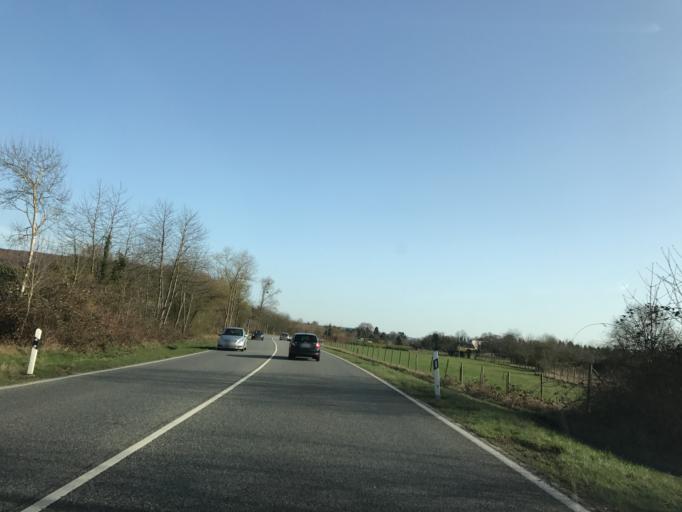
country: DE
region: Rheinland-Pfalz
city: Unkel
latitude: 50.5895
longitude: 7.2246
